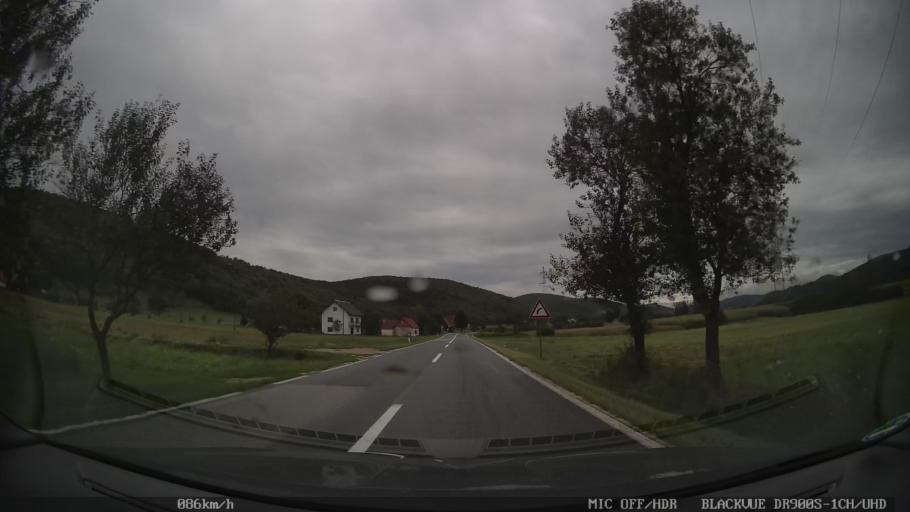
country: HR
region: Licko-Senjska
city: Brinje
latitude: 44.9193
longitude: 15.1494
